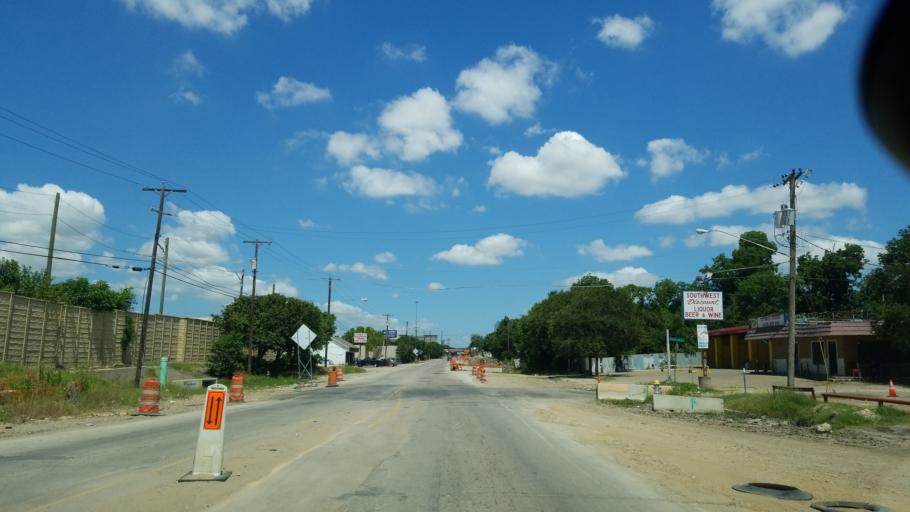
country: US
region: Texas
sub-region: Dallas County
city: Dallas
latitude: 32.7478
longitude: -96.7644
